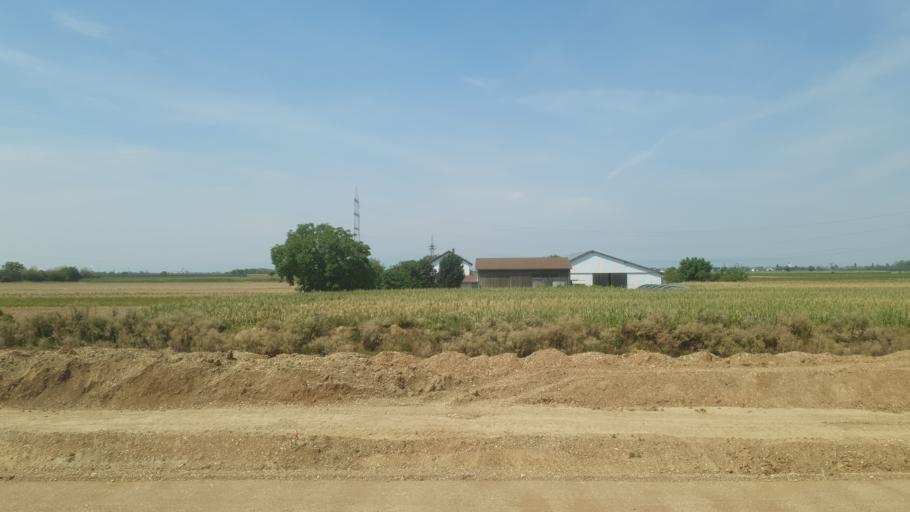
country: DE
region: Baden-Wuerttemberg
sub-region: Freiburg Region
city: Auggen
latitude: 47.7944
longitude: 7.5897
